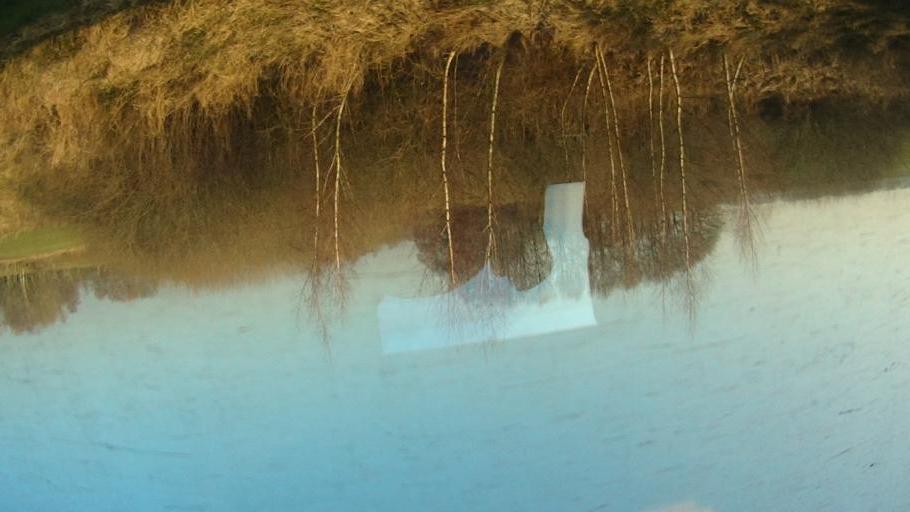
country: DE
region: Lower Saxony
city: Laar
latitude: 52.6206
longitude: 6.6969
